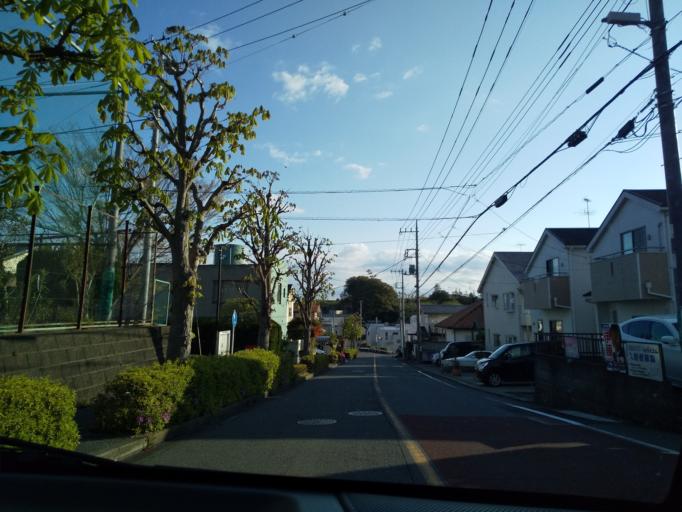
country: JP
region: Tokyo
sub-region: Machida-shi
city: Machida
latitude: 35.5702
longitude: 139.4591
